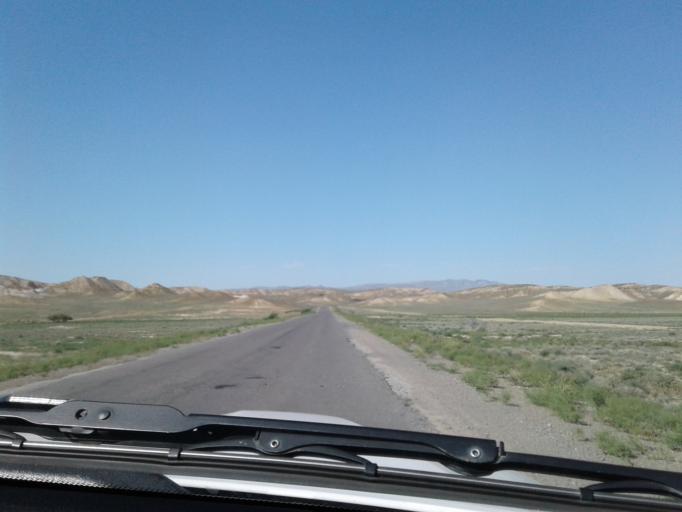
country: TM
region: Balkan
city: Magtymguly
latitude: 38.6691
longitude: 56.2896
